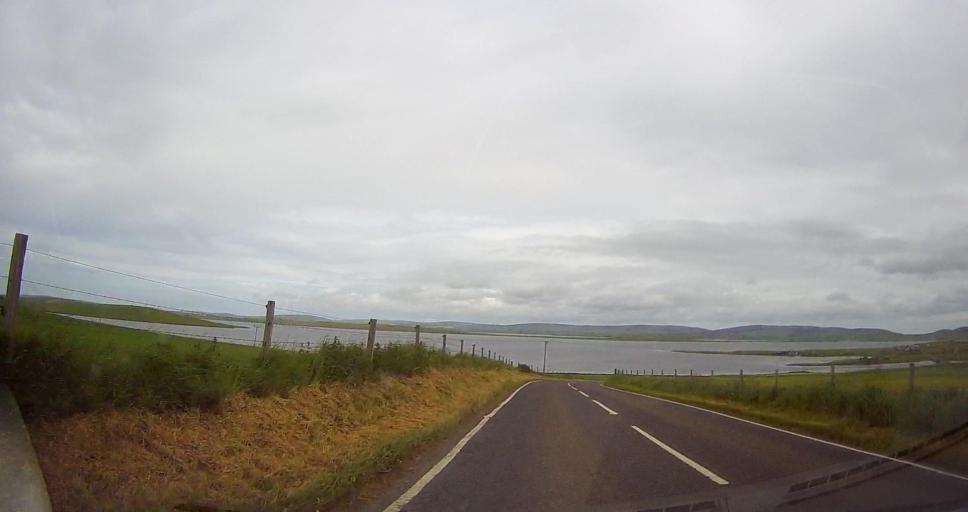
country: GB
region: Scotland
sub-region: Orkney Islands
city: Stromness
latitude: 58.9800
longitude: -3.2632
